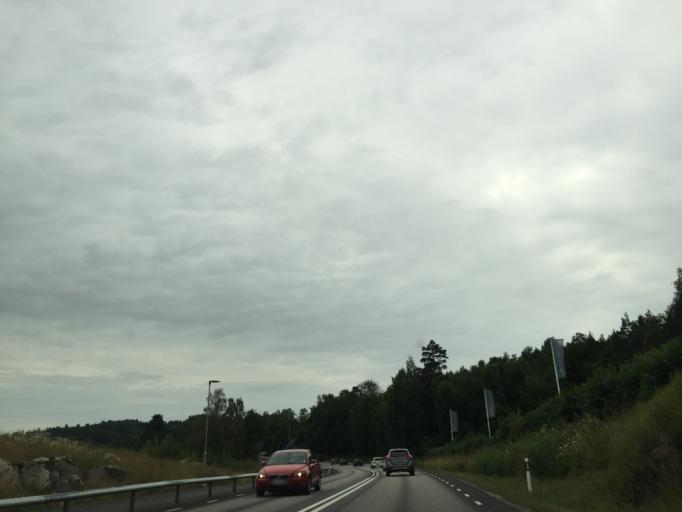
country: SE
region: Vaestra Goetaland
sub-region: Tjorns Kommun
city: Myggenas
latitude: 58.0542
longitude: 11.7576
